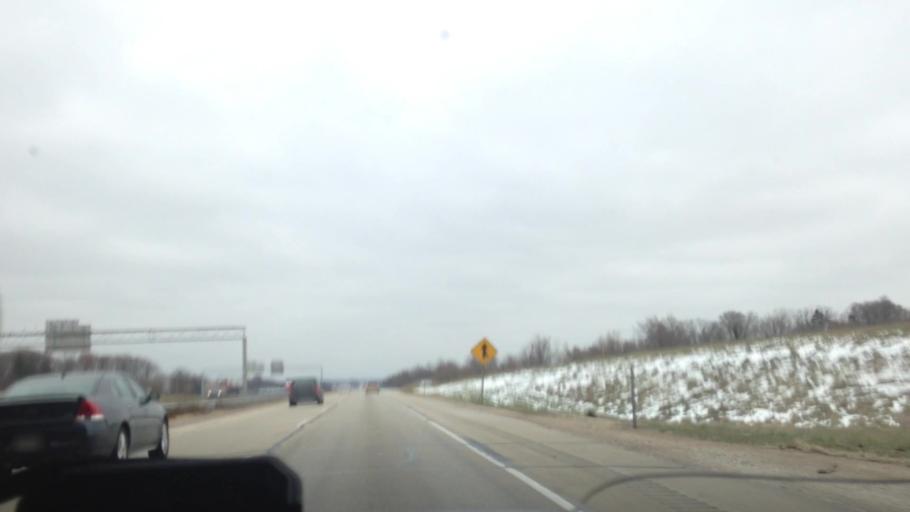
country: US
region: Wisconsin
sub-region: Washington County
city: Slinger
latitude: 43.3244
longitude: -88.2511
